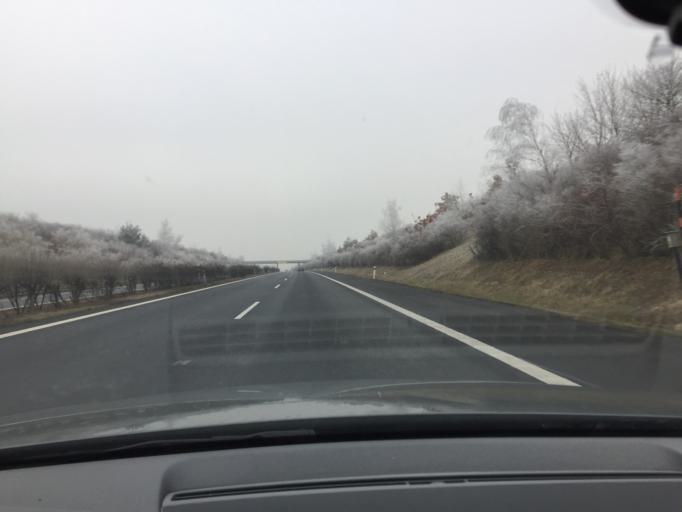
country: CZ
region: Ustecky
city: Roudnice nad Labem
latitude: 50.4142
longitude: 14.2141
